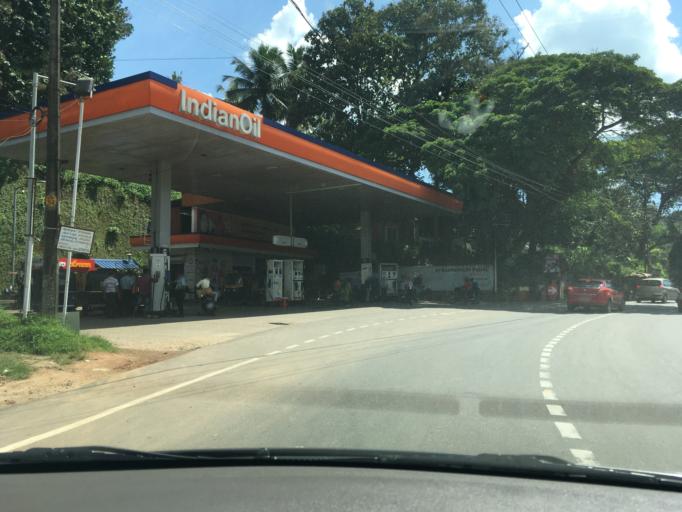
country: IN
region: Kerala
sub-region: Thiruvananthapuram
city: Nedumangad
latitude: 8.6047
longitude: 76.9985
